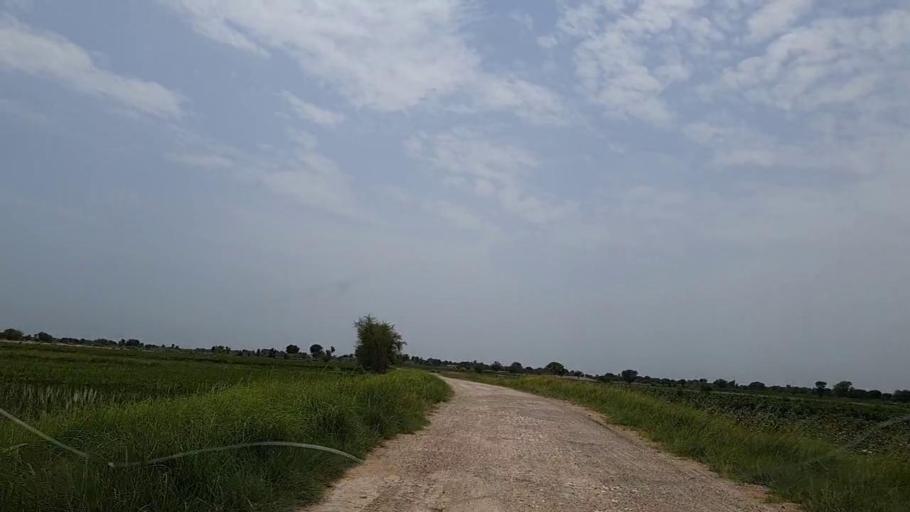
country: PK
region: Sindh
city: Tharu Shah
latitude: 26.9129
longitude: 68.0798
